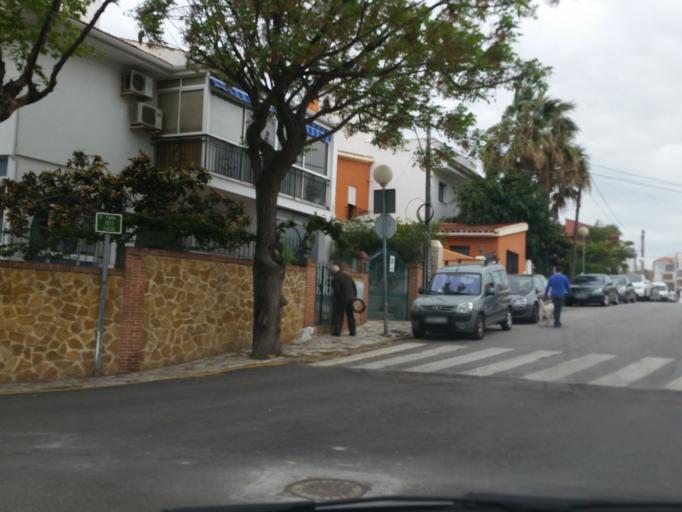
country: ES
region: Andalusia
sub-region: Provincia de Malaga
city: Fuengirola
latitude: 36.5616
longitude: -4.6171
